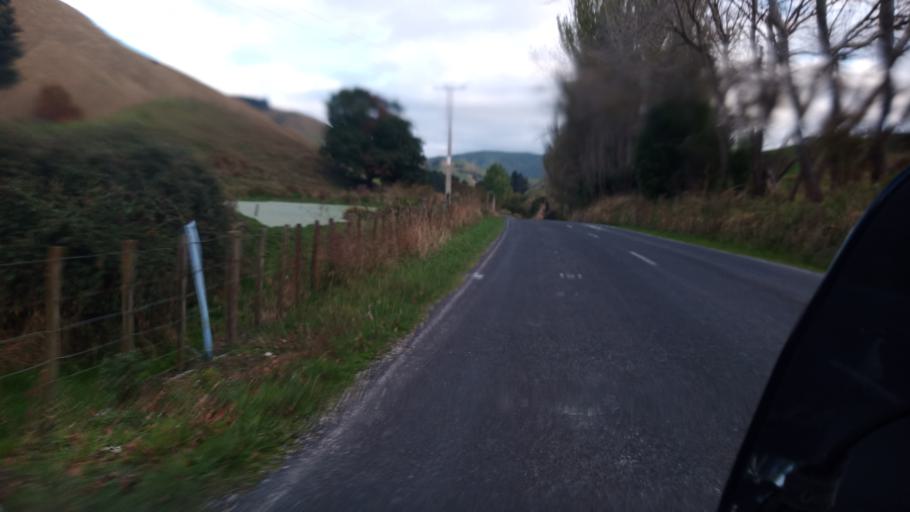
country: NZ
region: Gisborne
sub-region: Gisborne District
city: Gisborne
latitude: -38.5875
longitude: 177.7616
